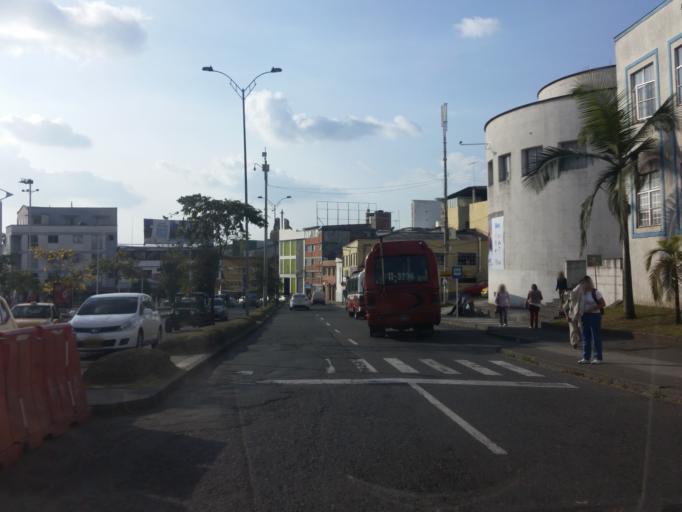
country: CO
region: Caldas
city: Manizales
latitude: 5.0632
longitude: -75.4998
